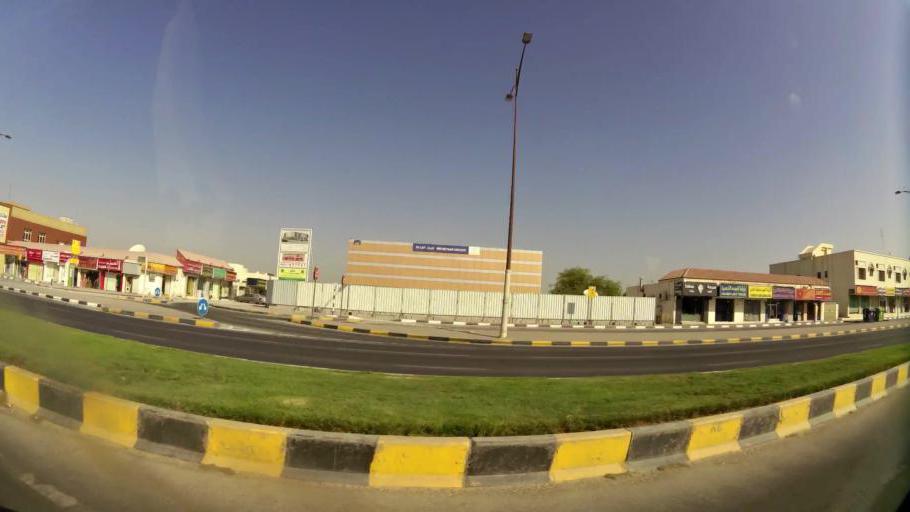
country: AE
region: Ash Shariqah
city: Sharjah
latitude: 25.3370
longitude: 55.4265
